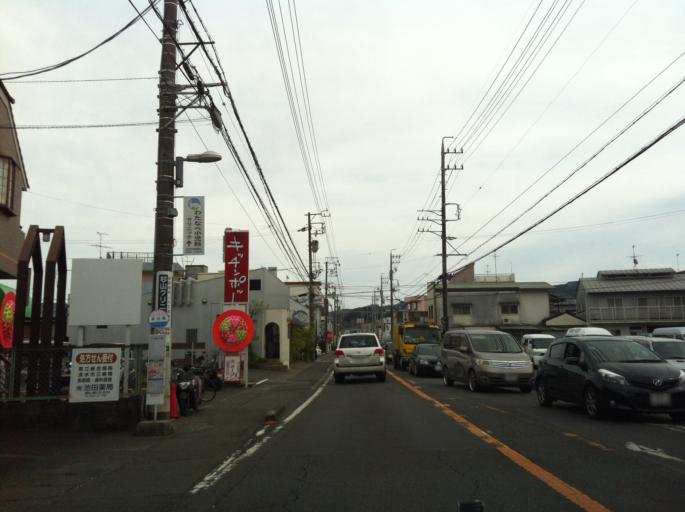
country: JP
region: Shizuoka
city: Shizuoka-shi
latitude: 35.0092
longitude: 138.4638
